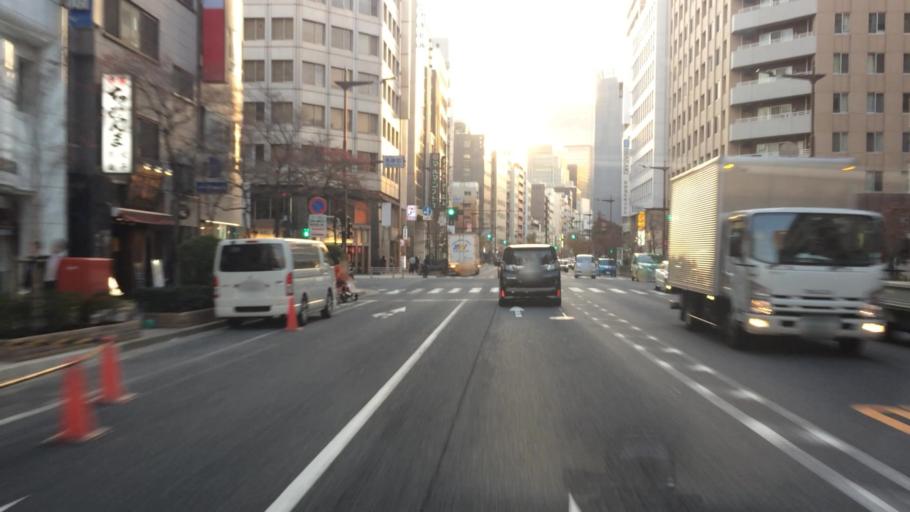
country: JP
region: Tokyo
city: Tokyo
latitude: 35.6934
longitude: 139.7824
